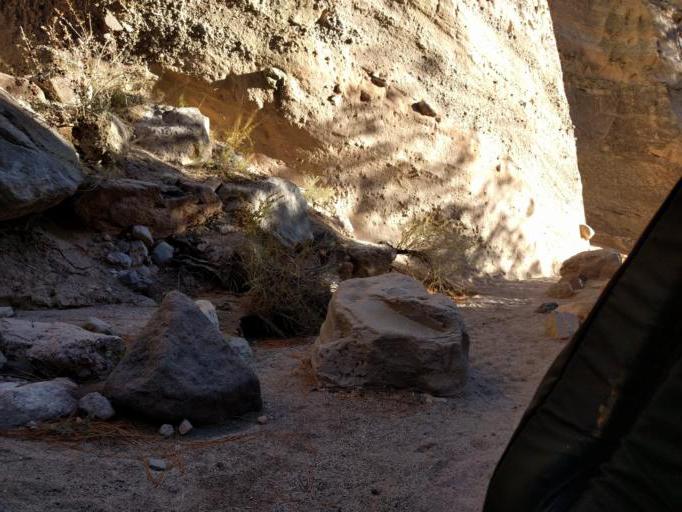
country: US
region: New Mexico
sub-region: Sandoval County
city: Santo Domingo Pueblo
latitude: 35.6626
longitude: -106.4061
